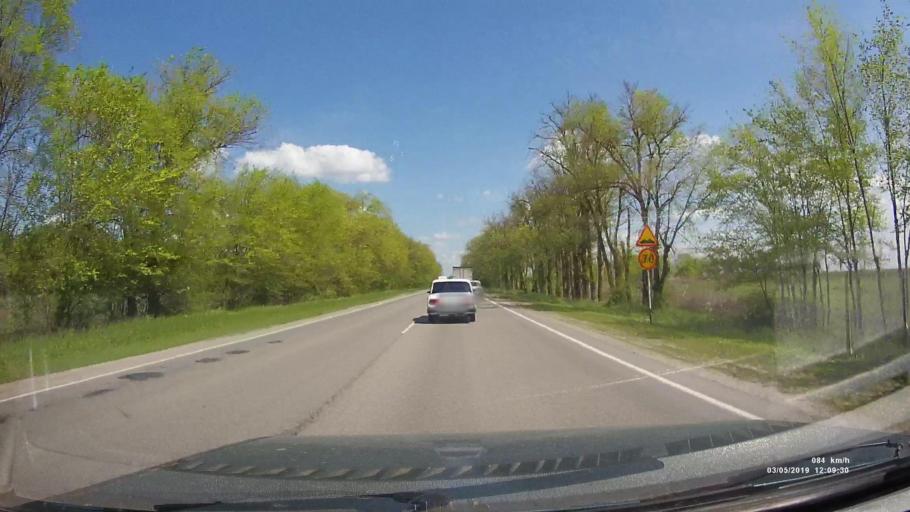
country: RU
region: Rostov
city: Bagayevskaya
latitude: 47.2950
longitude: 40.5170
